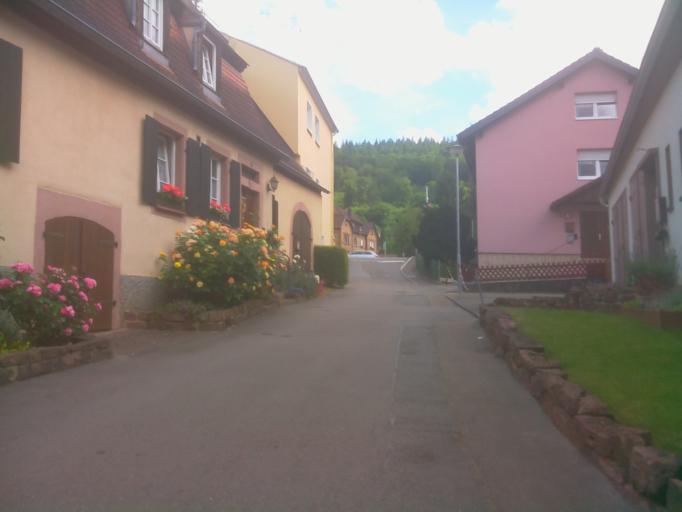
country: DE
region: Baden-Wuerttemberg
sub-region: Karlsruhe Region
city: Neckargemund
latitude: 49.3935
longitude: 8.7818
